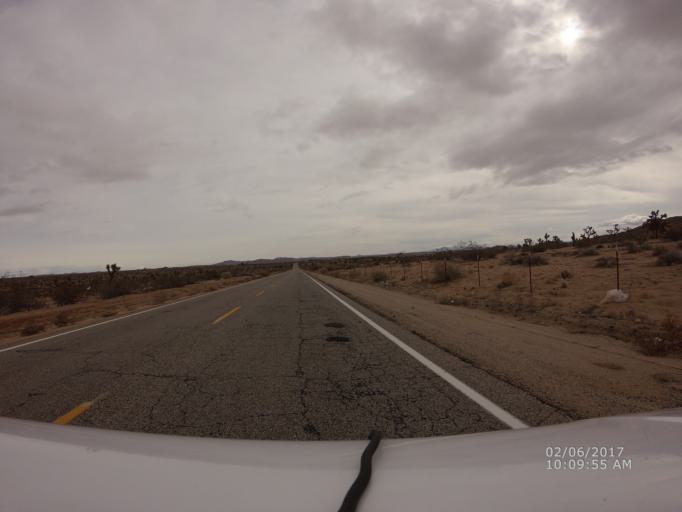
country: US
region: California
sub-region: Los Angeles County
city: Lake Los Angeles
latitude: 34.6903
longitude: -117.7875
